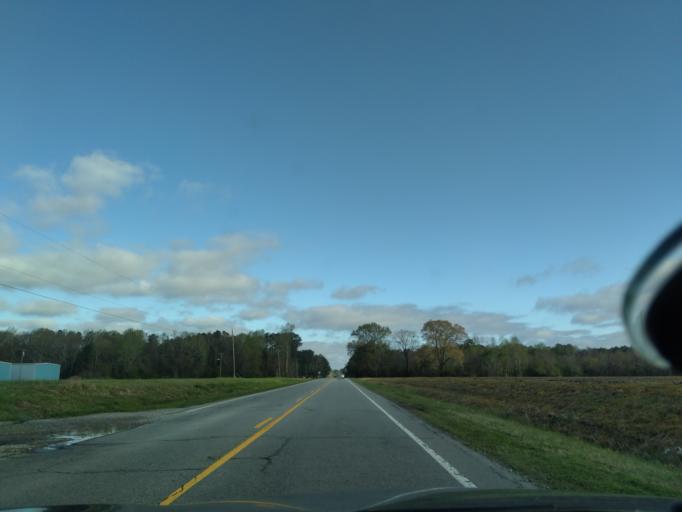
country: US
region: North Carolina
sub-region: Washington County
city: Plymouth
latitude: 36.0163
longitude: -76.7783
